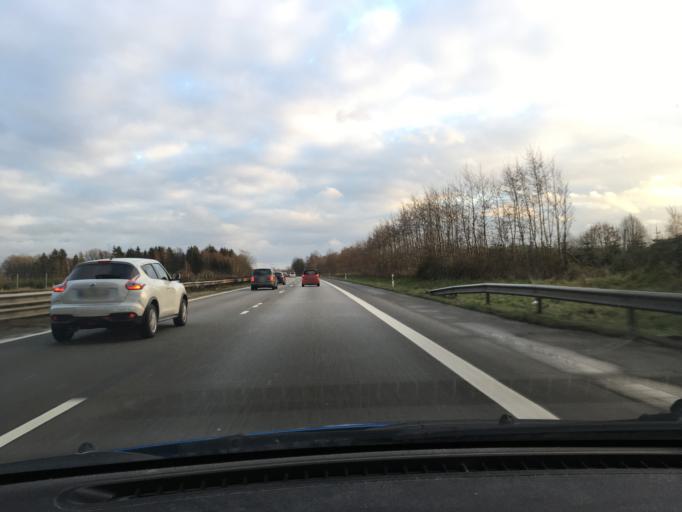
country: DE
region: Schleswig-Holstein
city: Seeth-Ekholt
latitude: 53.7283
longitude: 9.7282
